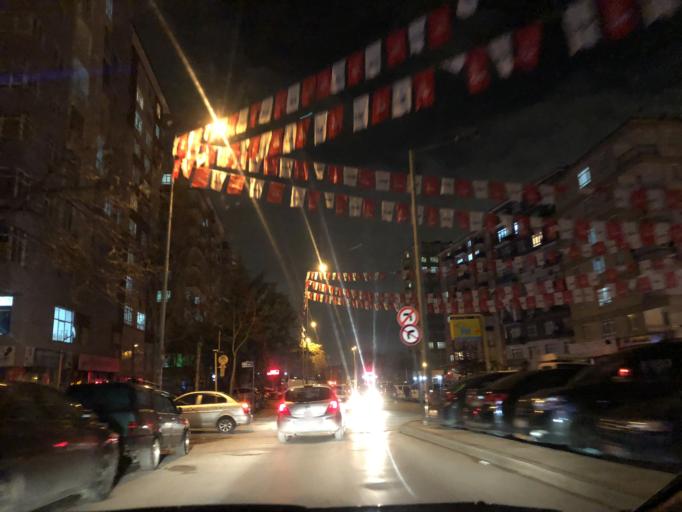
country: TR
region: Ankara
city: Batikent
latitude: 39.9650
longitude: 32.7958
